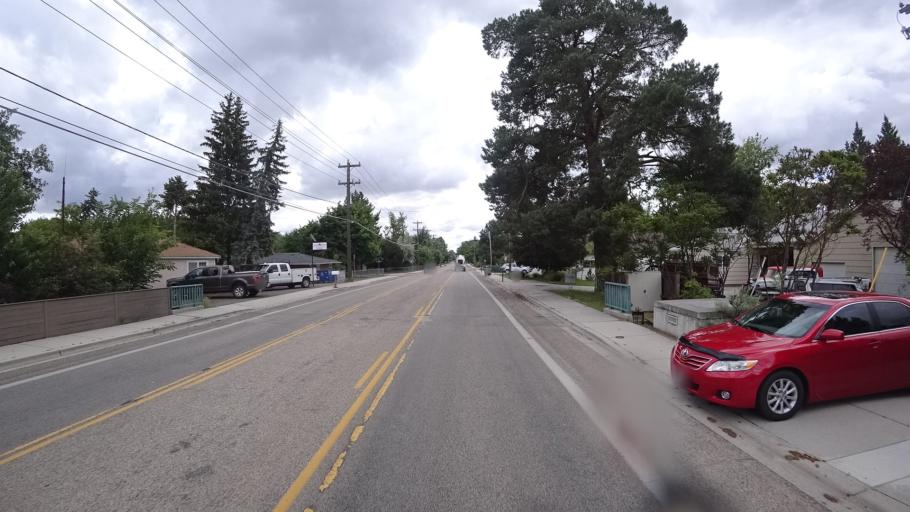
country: US
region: Idaho
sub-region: Ada County
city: Garden City
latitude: 43.6516
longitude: -116.2334
